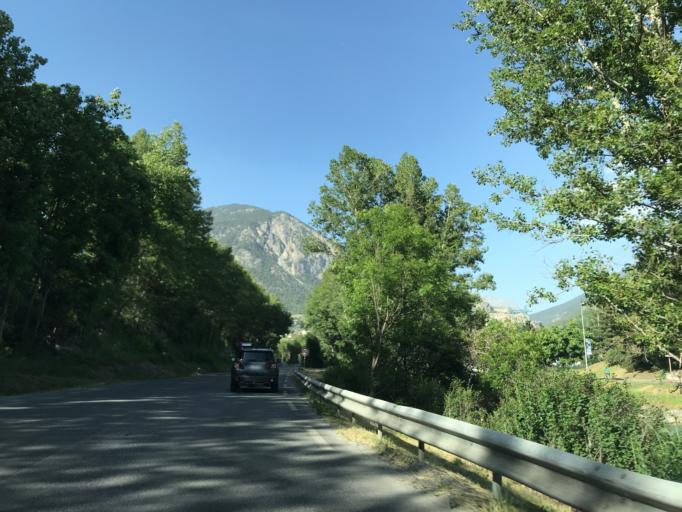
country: FR
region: Provence-Alpes-Cote d'Azur
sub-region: Departement des Hautes-Alpes
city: Villar-Saint-Pancrace
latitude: 44.8894
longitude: 6.6269
